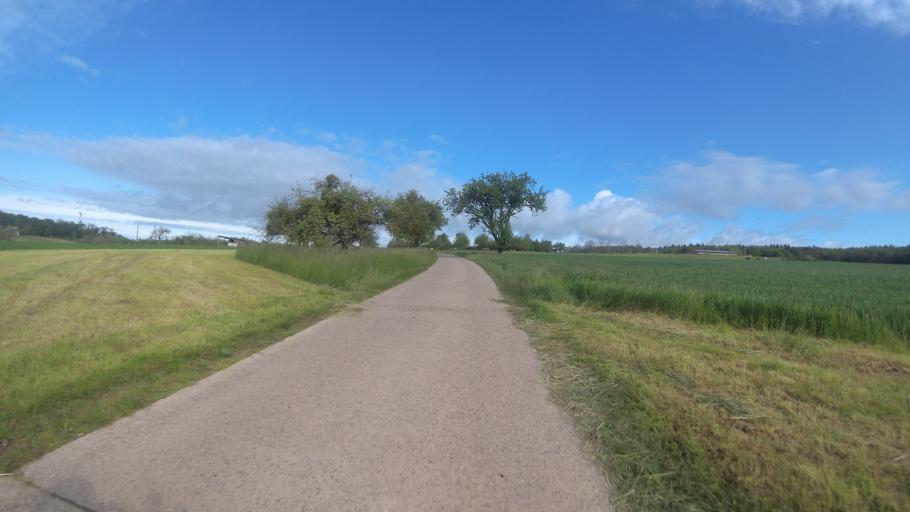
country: DE
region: Saarland
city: Mettlach
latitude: 49.4281
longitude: 6.5600
